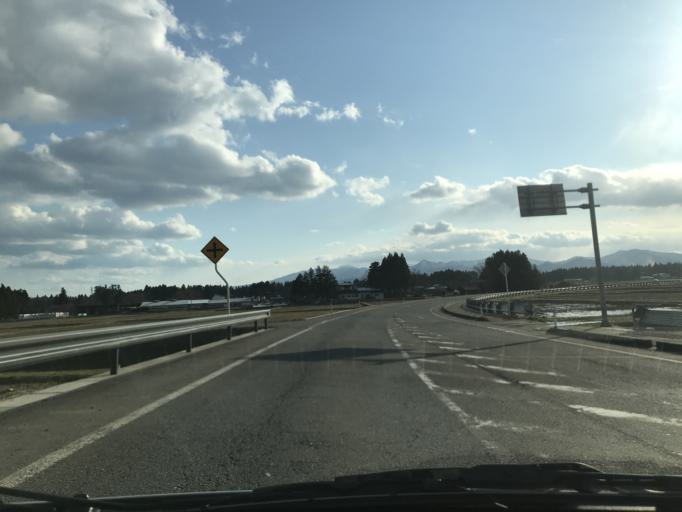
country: JP
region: Iwate
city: Hanamaki
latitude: 39.3372
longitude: 141.0476
